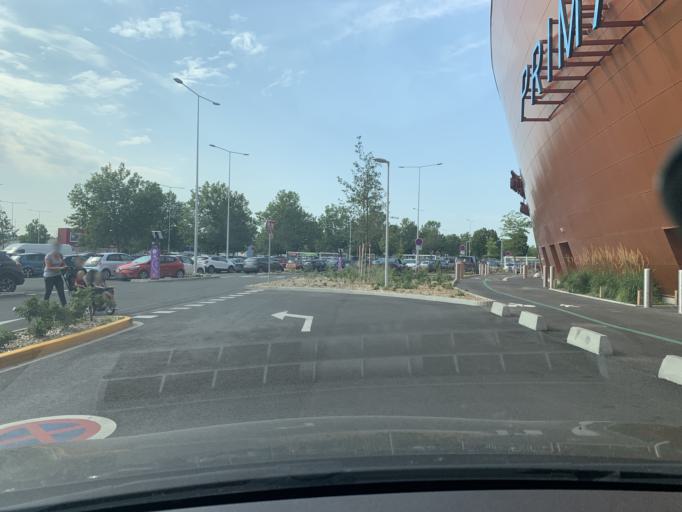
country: FR
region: Nord-Pas-de-Calais
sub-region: Departement du Pas-de-Calais
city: Noyelles-Godault
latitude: 50.4132
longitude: 2.9796
